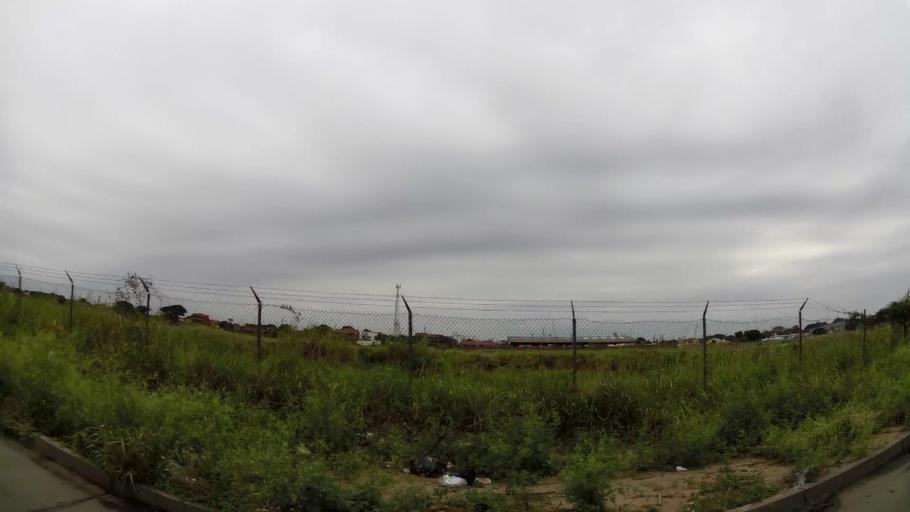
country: BO
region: Santa Cruz
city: Santa Cruz de la Sierra
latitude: -17.8093
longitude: -63.1718
